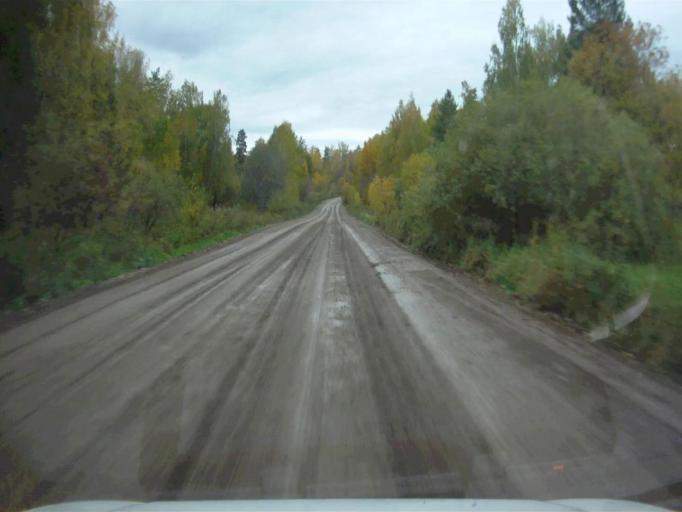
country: RU
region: Chelyabinsk
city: Nyazepetrovsk
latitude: 56.1089
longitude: 59.3768
